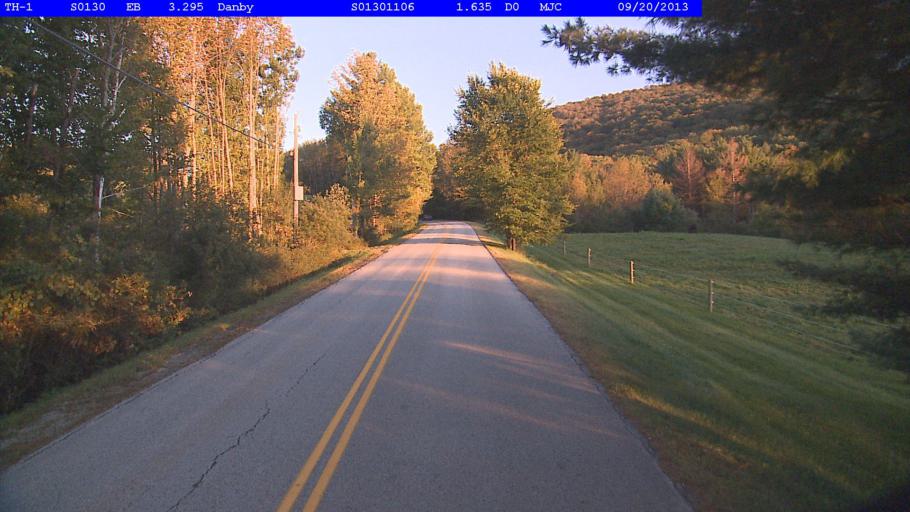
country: US
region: New York
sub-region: Washington County
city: Granville
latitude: 43.3656
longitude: -73.0939
